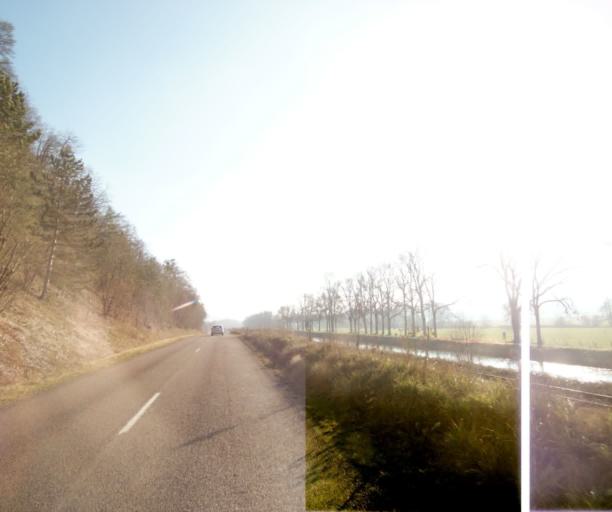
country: FR
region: Champagne-Ardenne
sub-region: Departement de la Haute-Marne
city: Chevillon
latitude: 48.5097
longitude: 5.1224
